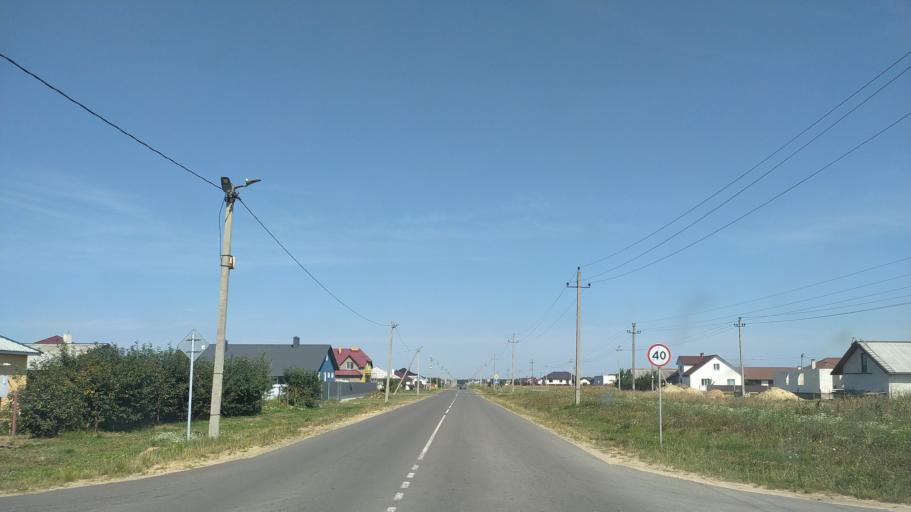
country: BY
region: Brest
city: Byaroza
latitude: 52.5164
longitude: 24.9726
